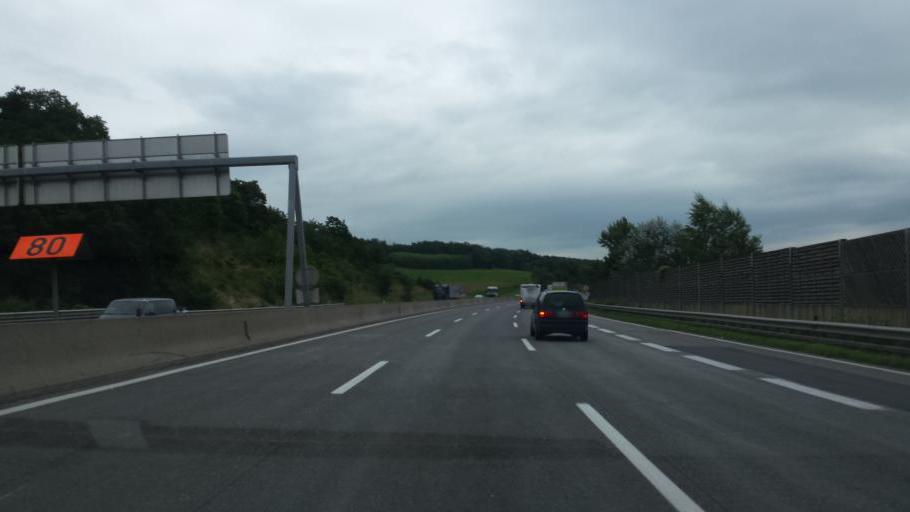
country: AT
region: Lower Austria
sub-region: Politischer Bezirk Melk
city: Melk
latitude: 48.2155
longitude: 15.3540
